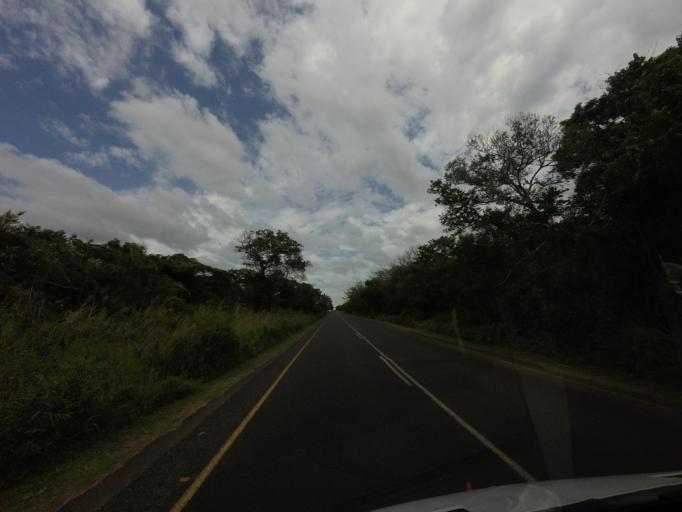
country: ZA
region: KwaZulu-Natal
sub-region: uMkhanyakude District Municipality
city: Mtubatuba
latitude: -28.3737
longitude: 32.3956
